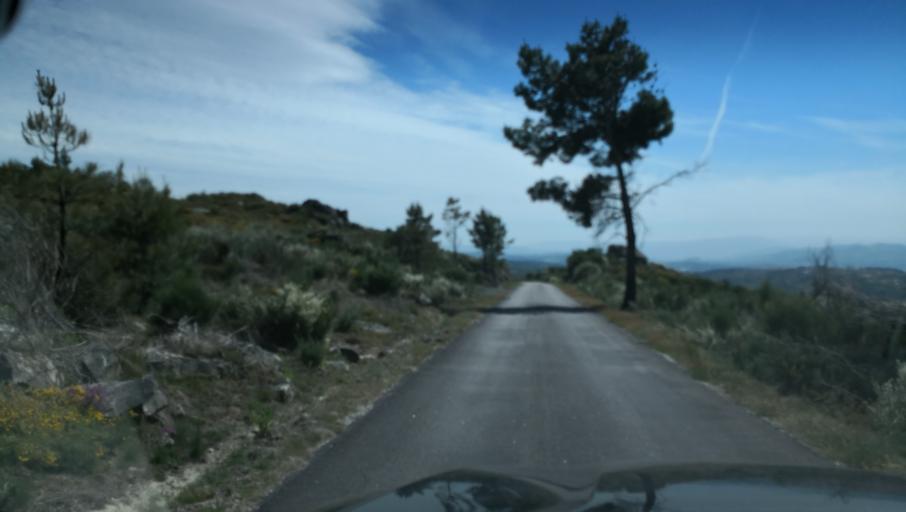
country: PT
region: Vila Real
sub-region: Vila Real
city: Vila Real
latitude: 41.3694
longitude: -7.6995
